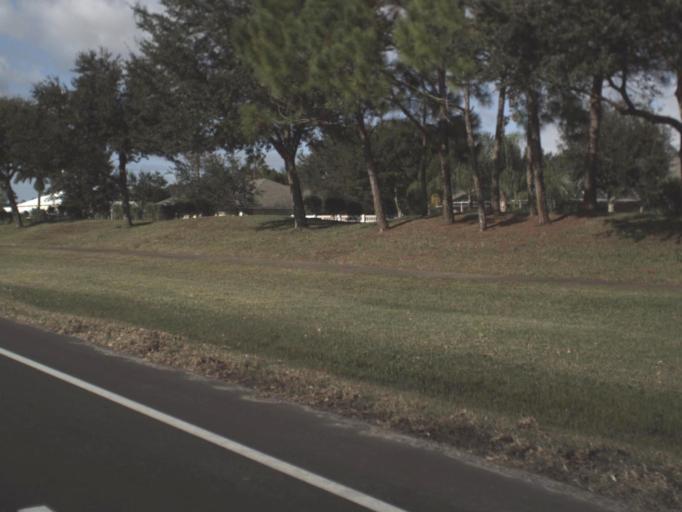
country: US
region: Florida
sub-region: Volusia County
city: Port Orange
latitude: 29.1350
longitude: -81.0507
